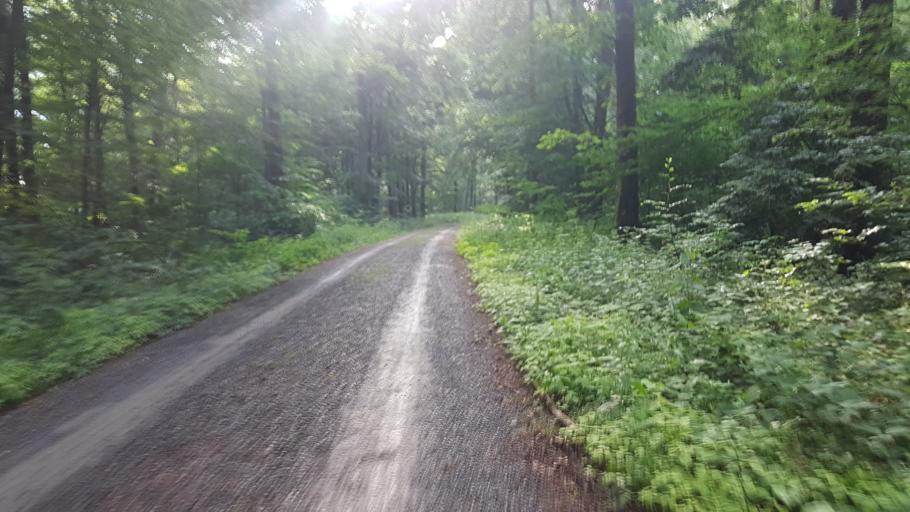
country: DE
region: Baden-Wuerttemberg
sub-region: Regierungsbezirk Stuttgart
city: Zaberfeld
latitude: 49.0387
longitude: 8.9103
